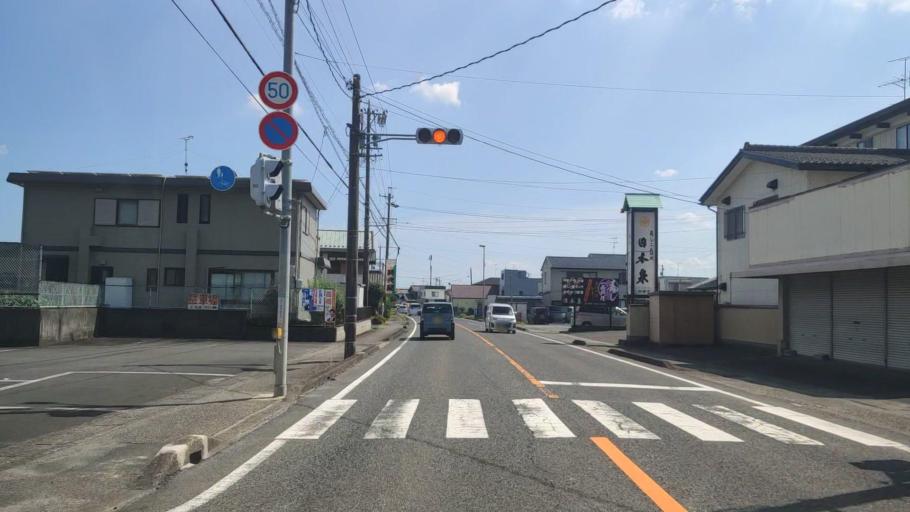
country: JP
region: Gifu
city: Godo
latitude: 35.4716
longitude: 136.6754
